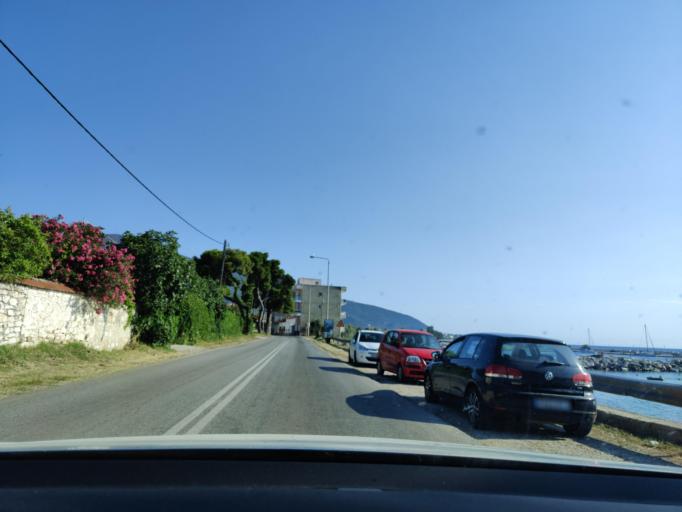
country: GR
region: East Macedonia and Thrace
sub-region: Nomos Kavalas
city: Prinos
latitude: 40.7114
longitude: 24.5340
